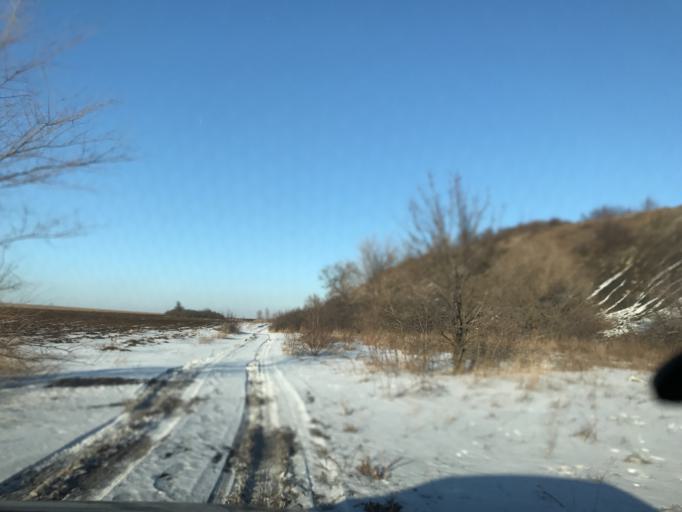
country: RU
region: Rostov
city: Staraya Stanitsa
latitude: 48.2384
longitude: 40.3943
